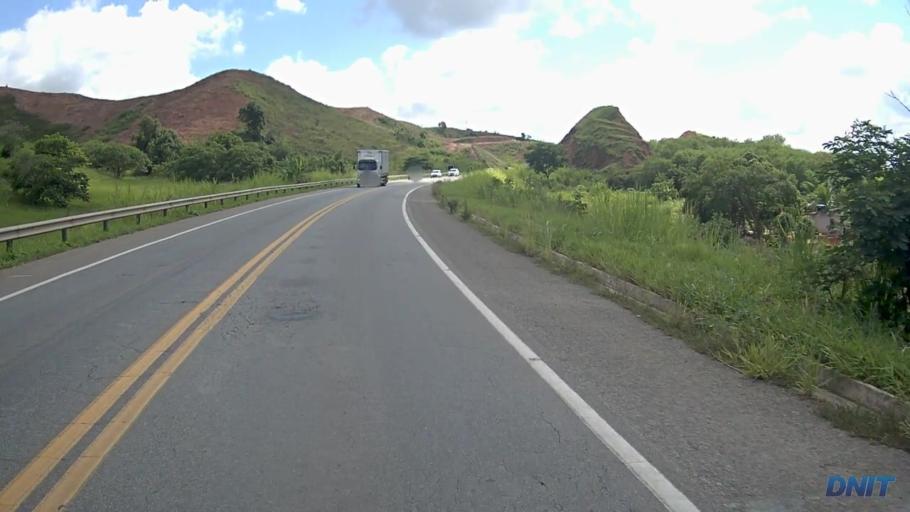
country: BR
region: Minas Gerais
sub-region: Belo Oriente
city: Belo Oriente
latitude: -19.1475
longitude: -42.2317
